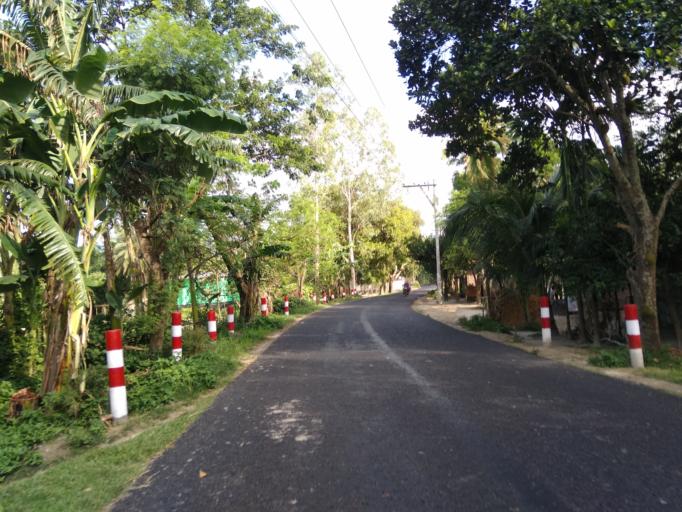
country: BD
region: Rangpur Division
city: Rangpur
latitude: 25.8439
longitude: 89.1126
